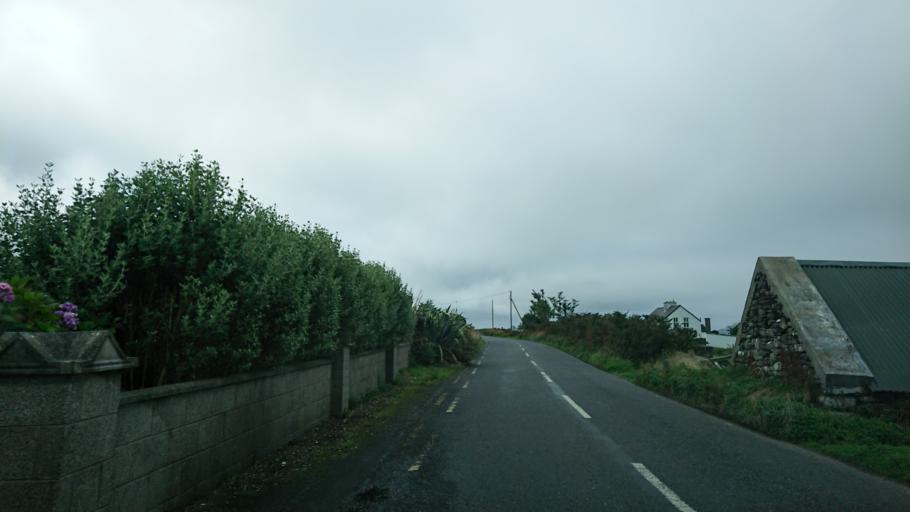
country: IE
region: Munster
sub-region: Ciarrai
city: Cahersiveen
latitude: 51.9328
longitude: -10.2559
